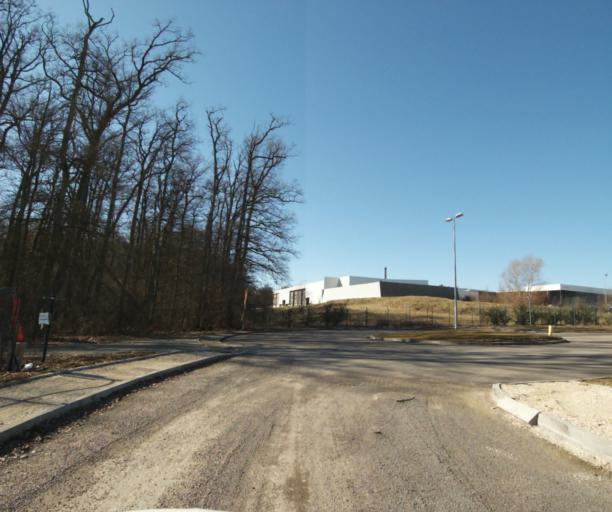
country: FR
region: Lorraine
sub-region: Departement de Meurthe-et-Moselle
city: Fleville-devant-Nancy
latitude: 48.6063
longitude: 6.1962
